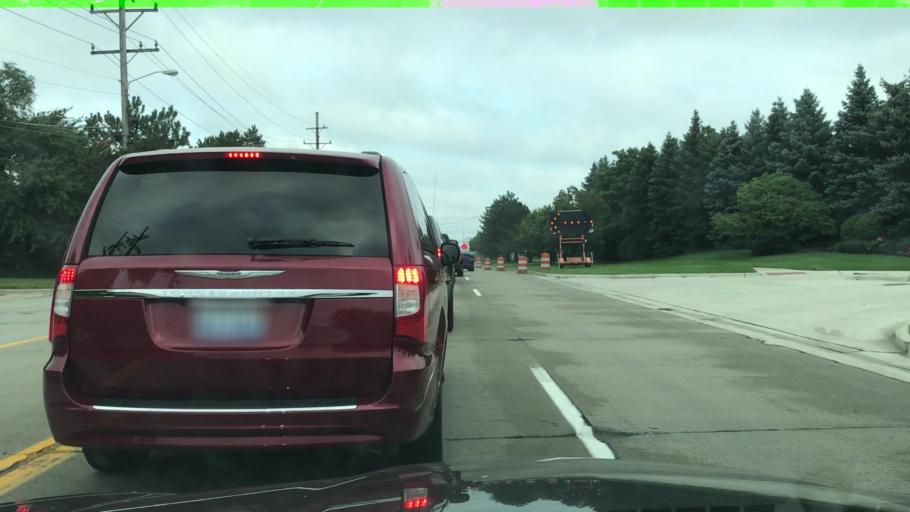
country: US
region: Michigan
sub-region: Macomb County
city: Sterling Heights
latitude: 42.5796
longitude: -83.0537
